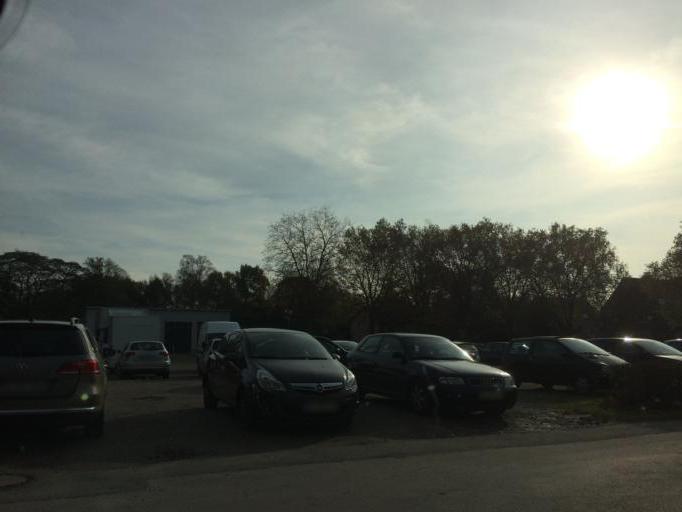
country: DE
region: North Rhine-Westphalia
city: Dorsten
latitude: 51.6636
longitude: 6.9682
